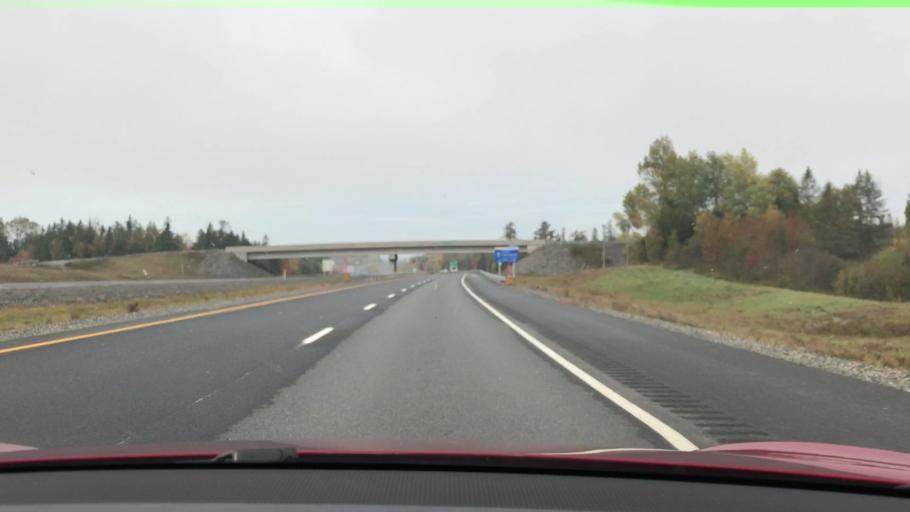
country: US
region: Maine
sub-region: Washington County
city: Calais
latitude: 45.2173
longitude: -67.2367
